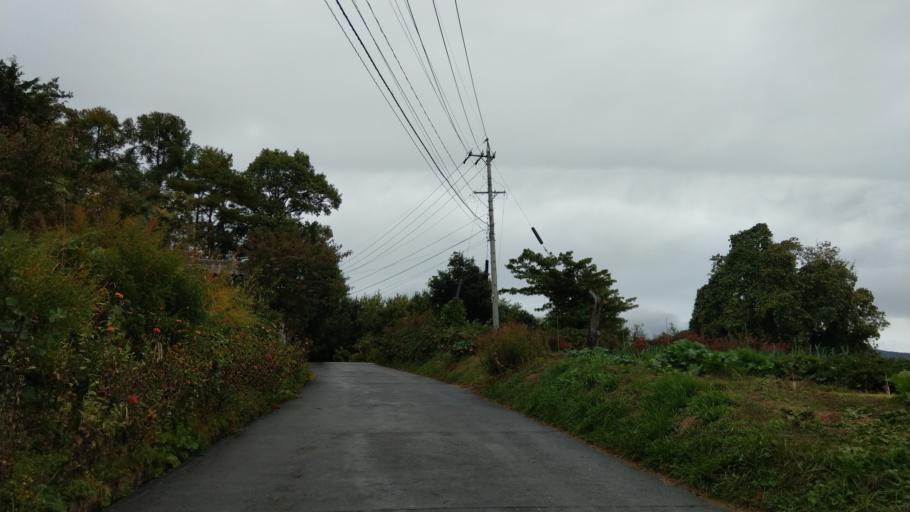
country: JP
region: Nagano
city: Komoro
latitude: 36.3576
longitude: 138.4244
